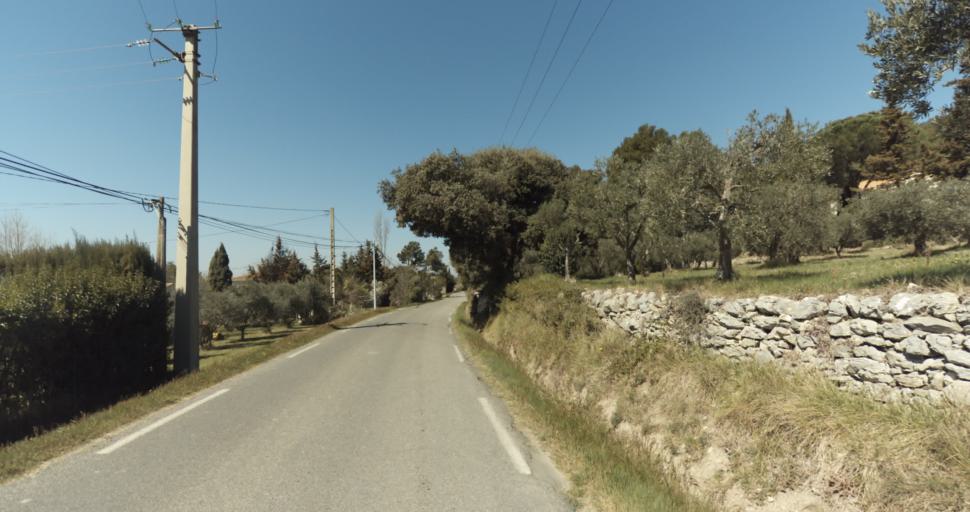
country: FR
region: Provence-Alpes-Cote d'Azur
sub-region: Departement des Bouches-du-Rhone
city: Pelissanne
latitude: 43.6133
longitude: 5.1716
